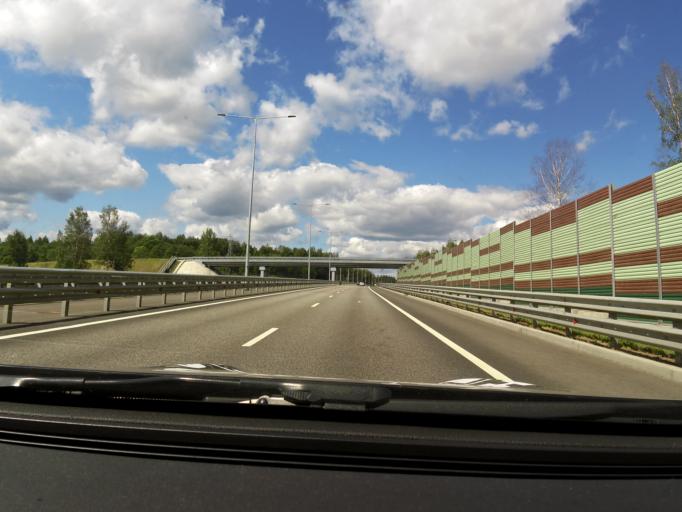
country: RU
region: Tverskaya
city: Vyshniy Volochek
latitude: 57.3753
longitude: 34.5933
